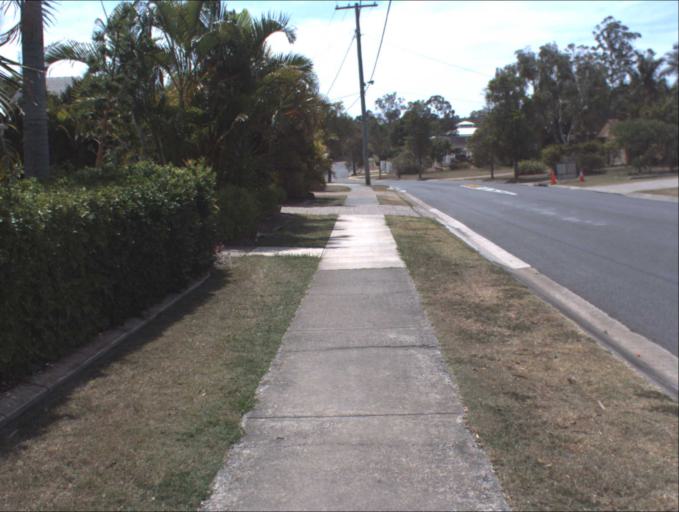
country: AU
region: Queensland
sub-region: Logan
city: Beenleigh
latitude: -27.6645
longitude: 153.2047
